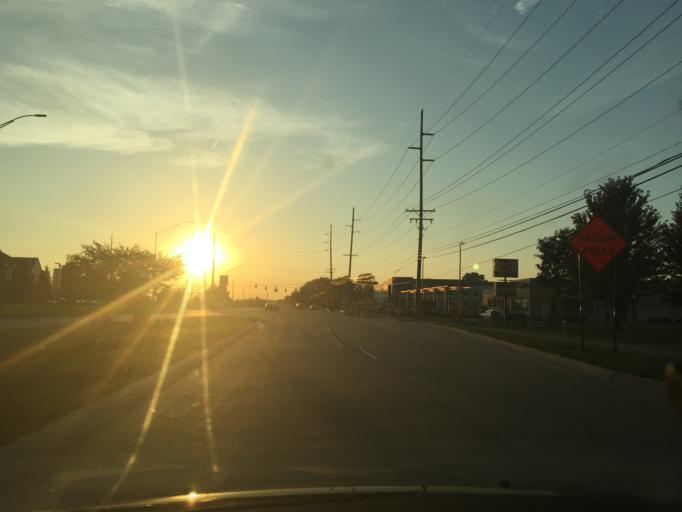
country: US
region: Michigan
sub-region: Oakland County
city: Auburn Hills
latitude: 42.6493
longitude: -83.2456
